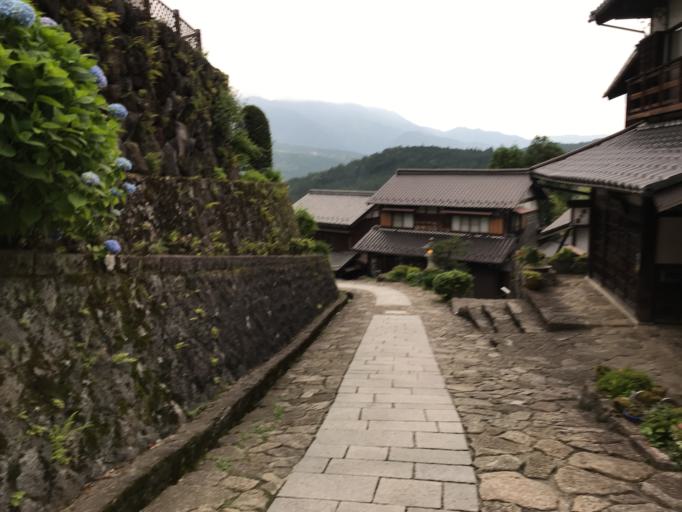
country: JP
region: Gifu
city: Nakatsugawa
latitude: 35.5255
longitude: 137.5659
